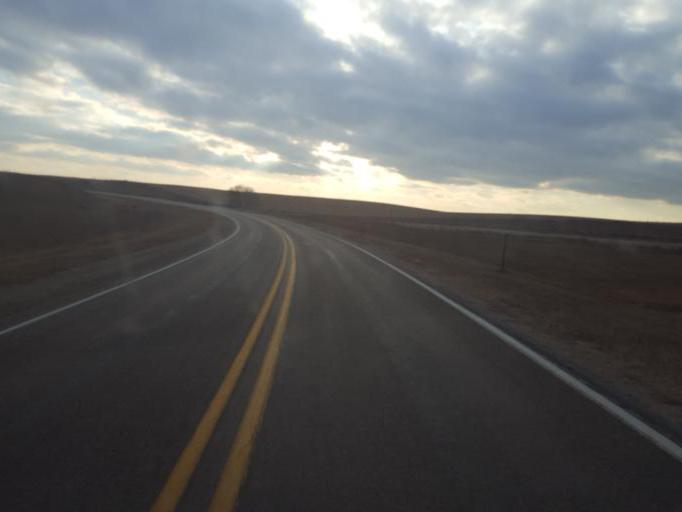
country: US
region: Nebraska
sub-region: Knox County
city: Bloomfield
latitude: 42.6119
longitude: -97.5219
